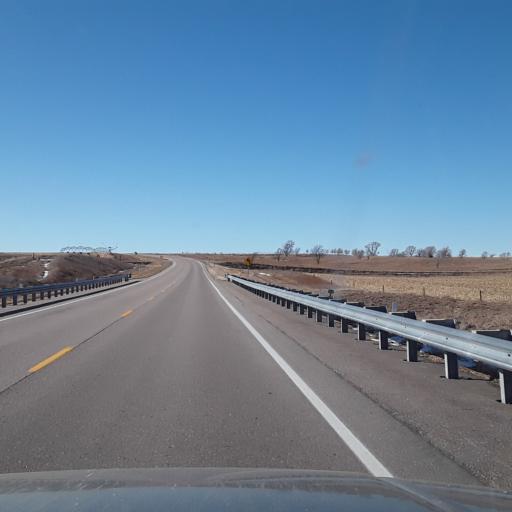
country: US
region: Nebraska
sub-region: Frontier County
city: Stockville
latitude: 40.7058
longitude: -100.2391
